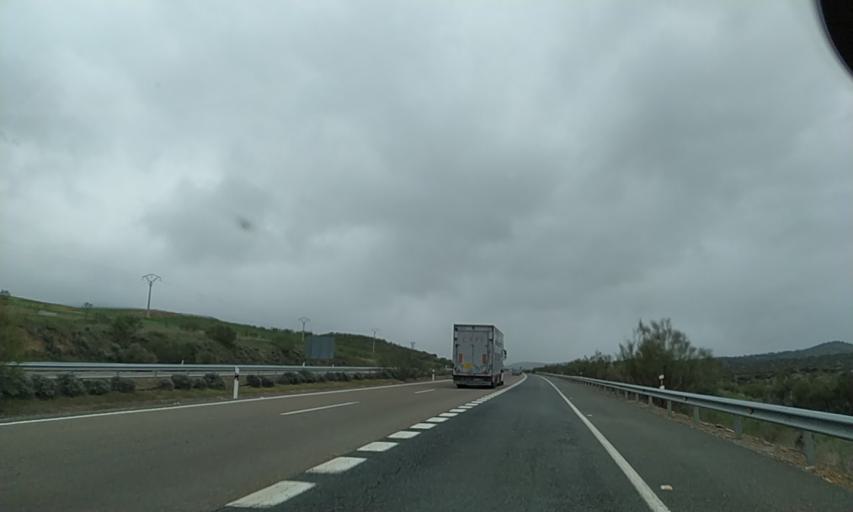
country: ES
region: Extremadura
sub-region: Provincia de Caceres
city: Riolobos
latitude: 39.8799
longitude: -6.2808
